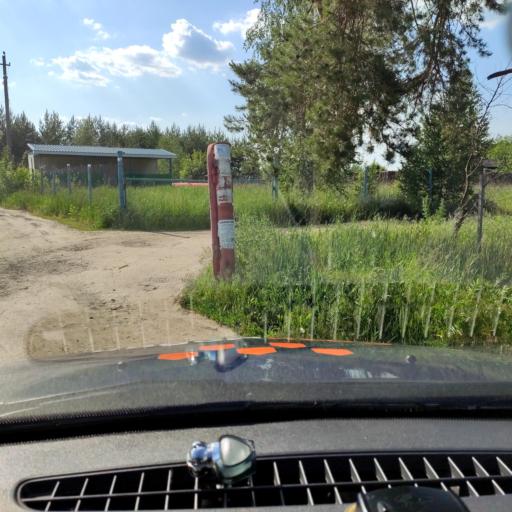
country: RU
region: Voronezj
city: Ramon'
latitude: 51.8922
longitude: 39.2068
